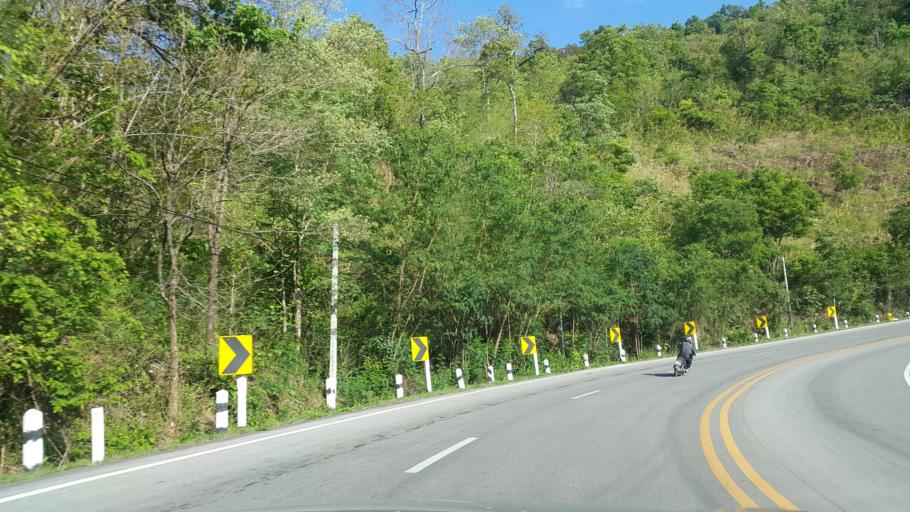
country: TH
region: Phayao
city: Phayao
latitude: 19.0874
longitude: 99.8107
